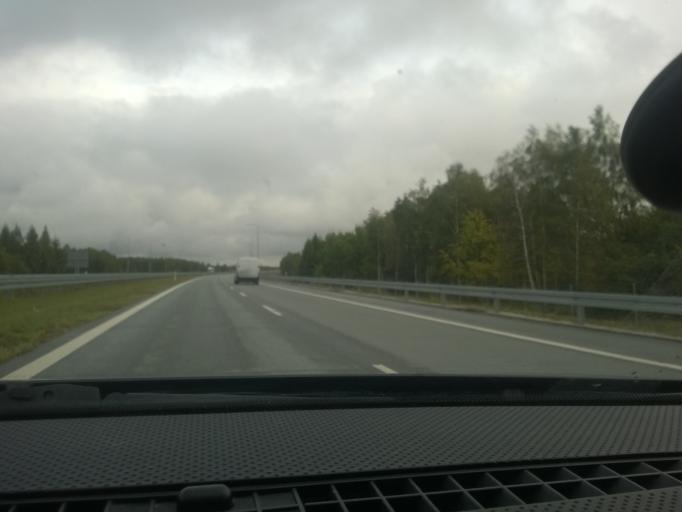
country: PL
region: Lodz Voivodeship
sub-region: Powiat zdunskowolski
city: Zapolice
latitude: 51.5984
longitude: 18.8635
